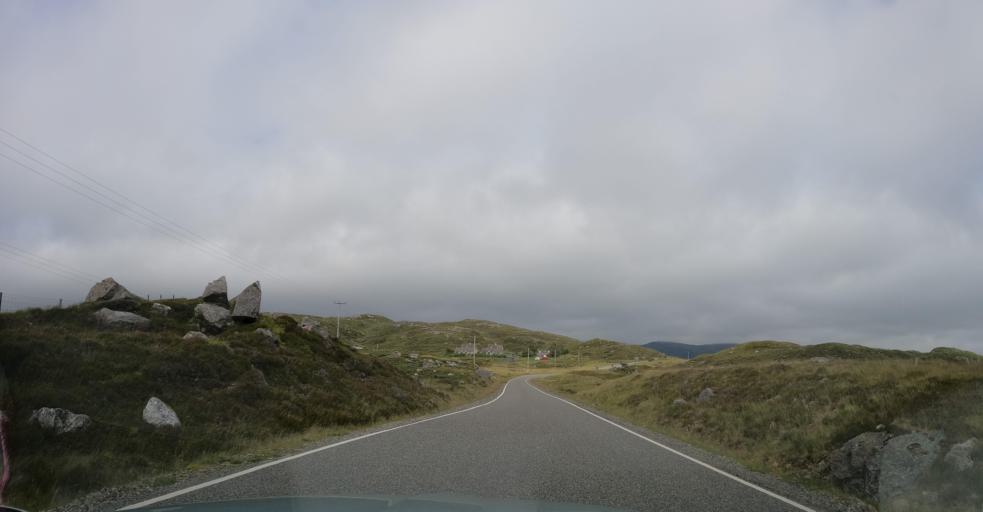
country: GB
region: Scotland
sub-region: Eilean Siar
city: Harris
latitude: 57.8872
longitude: -6.8104
